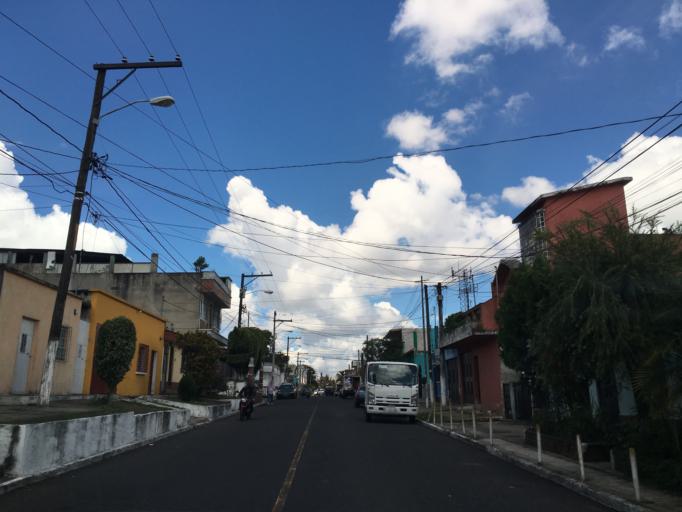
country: GT
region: Guatemala
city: Mixco
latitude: 14.6303
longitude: -90.5834
